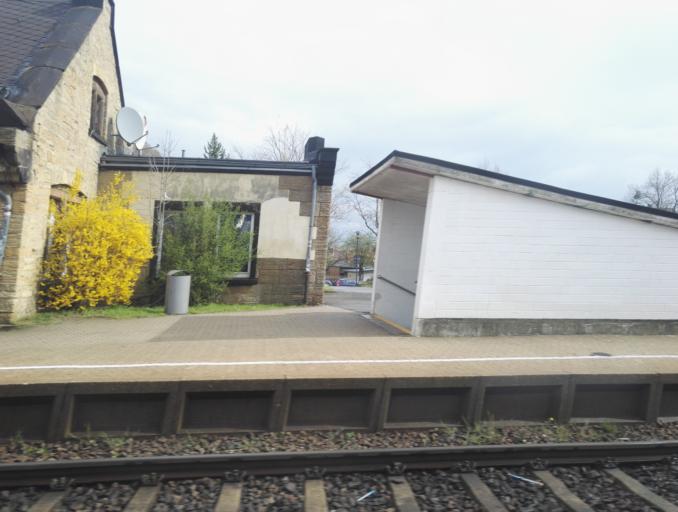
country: DE
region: Lower Saxony
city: Goslar
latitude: 51.9049
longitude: 10.4785
